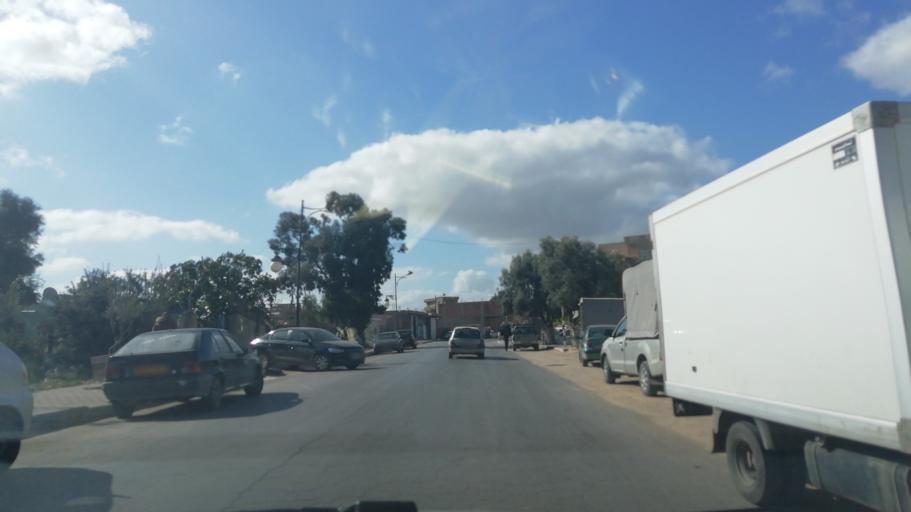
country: DZ
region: Relizane
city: Mazouna
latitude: 36.2714
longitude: 0.6327
